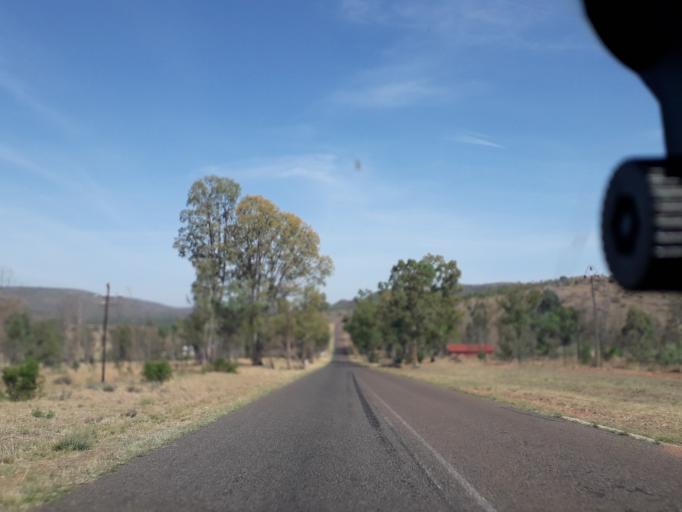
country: ZA
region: Limpopo
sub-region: Waterberg District Municipality
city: Warmbaths
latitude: -24.8364
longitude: 28.2332
